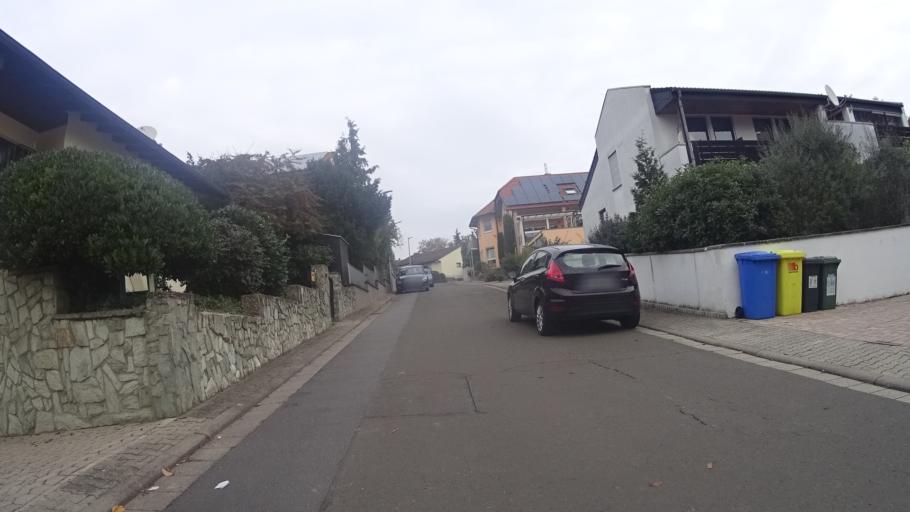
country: DE
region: Rheinland-Pfalz
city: Monsheim
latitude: 49.6384
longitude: 8.2029
